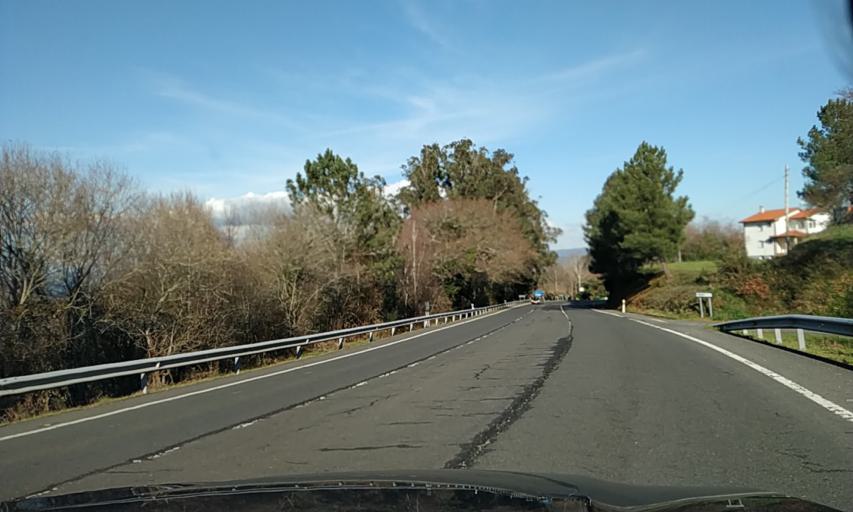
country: ES
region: Galicia
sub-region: Provincia de Pontevedra
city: Silleda
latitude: 42.6975
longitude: -8.3246
